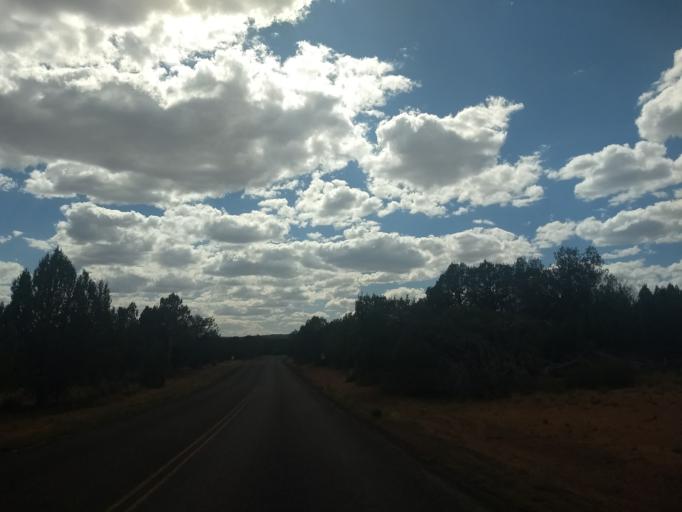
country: US
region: Utah
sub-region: Kane County
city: Kanab
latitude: 37.1462
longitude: -112.5526
